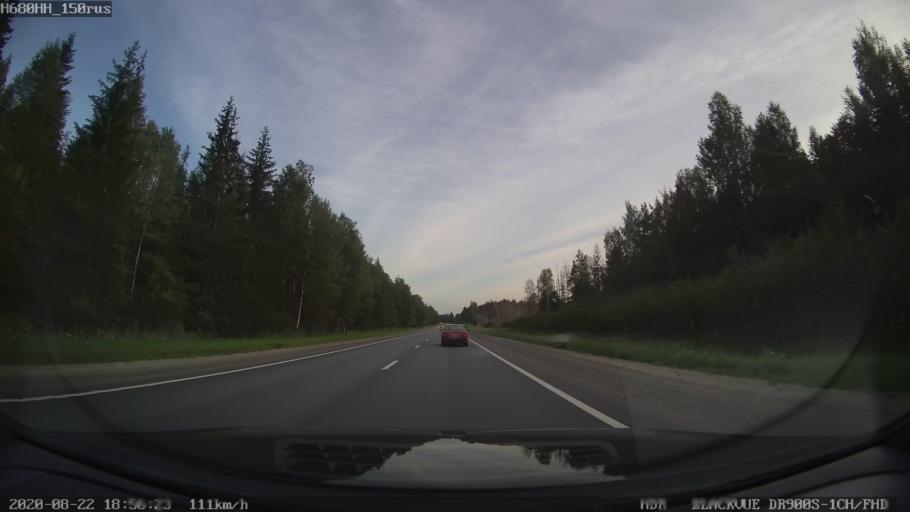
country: RU
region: Tverskaya
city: Rameshki
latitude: 57.1842
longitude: 36.0820
